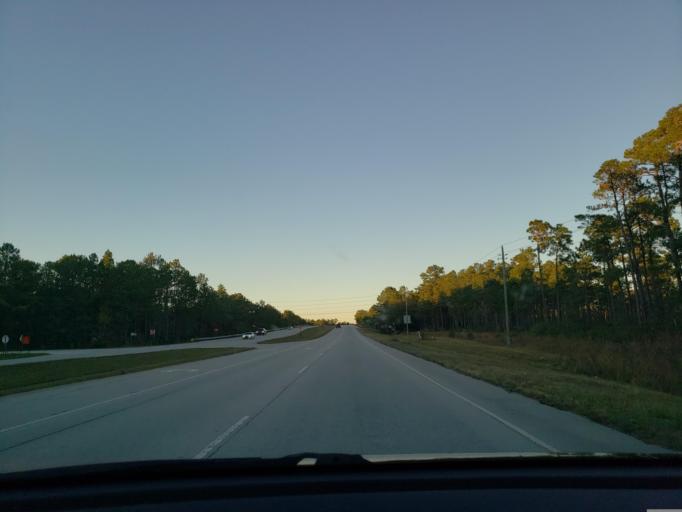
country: US
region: North Carolina
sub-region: Onslow County
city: Sneads Ferry
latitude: 34.6095
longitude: -77.4831
